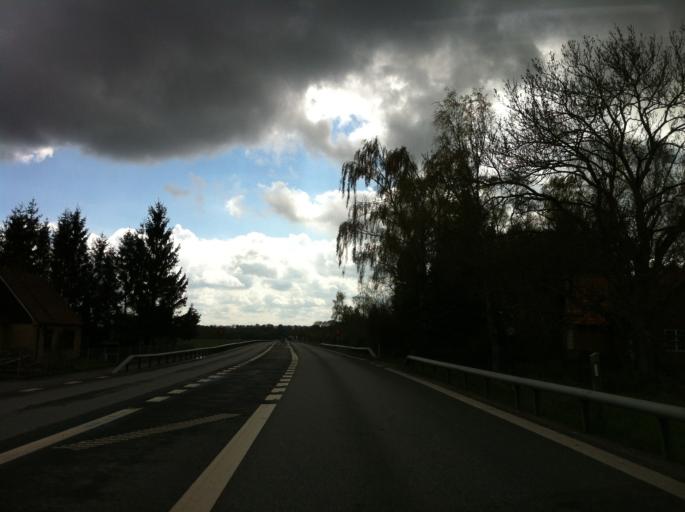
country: SE
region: Skane
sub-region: Hoors Kommun
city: Satofta
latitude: 55.9012
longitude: 13.5211
